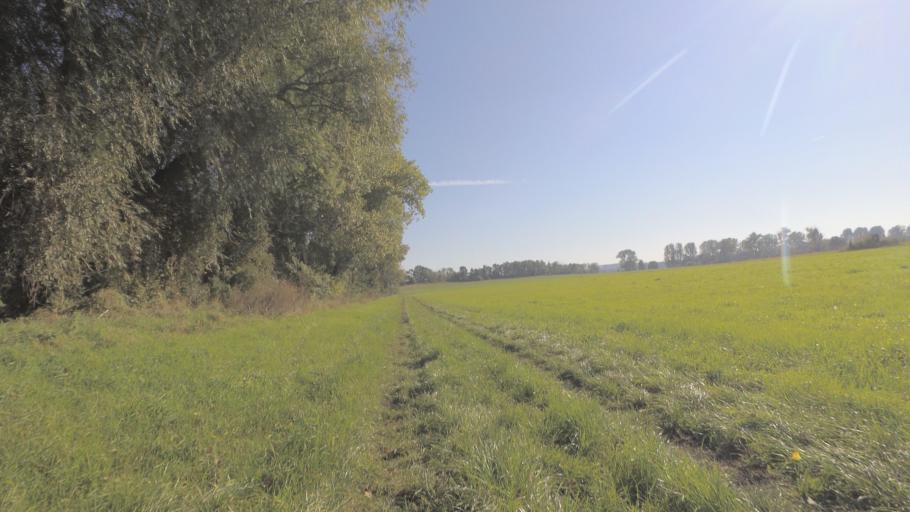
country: DE
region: Brandenburg
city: Rangsdorf
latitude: 52.2964
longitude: 13.3667
